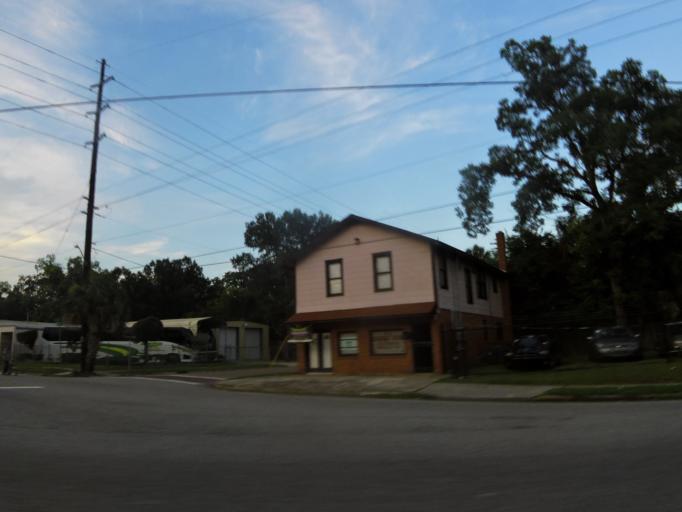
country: US
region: Florida
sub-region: Duval County
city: Jacksonville
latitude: 30.3601
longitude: -81.6761
